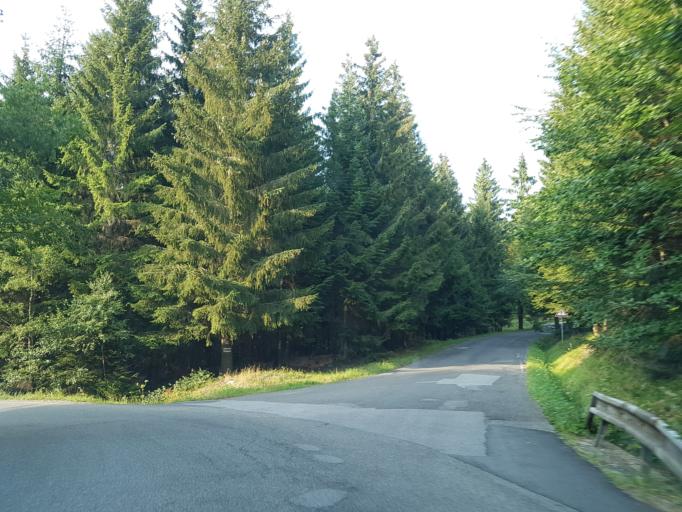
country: CZ
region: Liberecky
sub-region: Okres Jablonec nad Nisou
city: Jablonec nad Nisou
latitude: 50.7100
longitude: 15.2024
